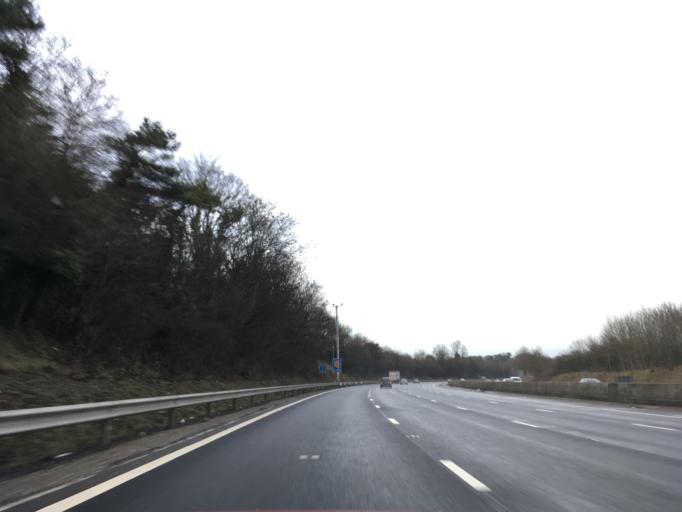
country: GB
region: England
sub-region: Worcestershire
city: Droitwich
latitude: 52.2618
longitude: -2.1375
